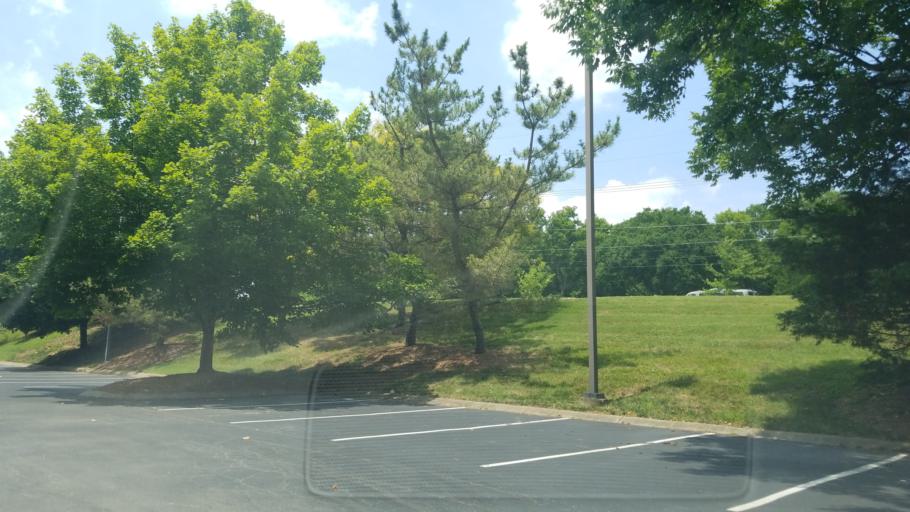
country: US
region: Tennessee
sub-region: Williamson County
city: Brentwood
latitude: 36.0385
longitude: -86.8101
